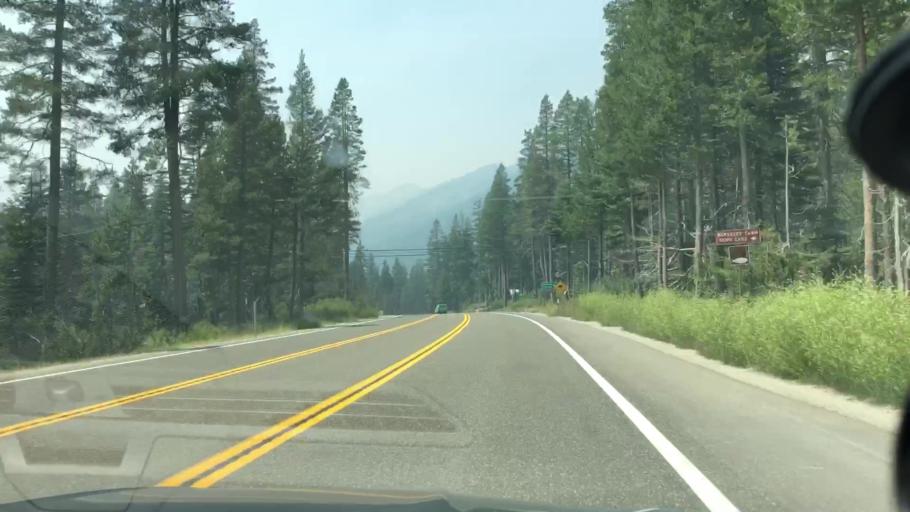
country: US
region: California
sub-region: El Dorado County
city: South Lake Tahoe
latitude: 38.8241
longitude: -120.0427
